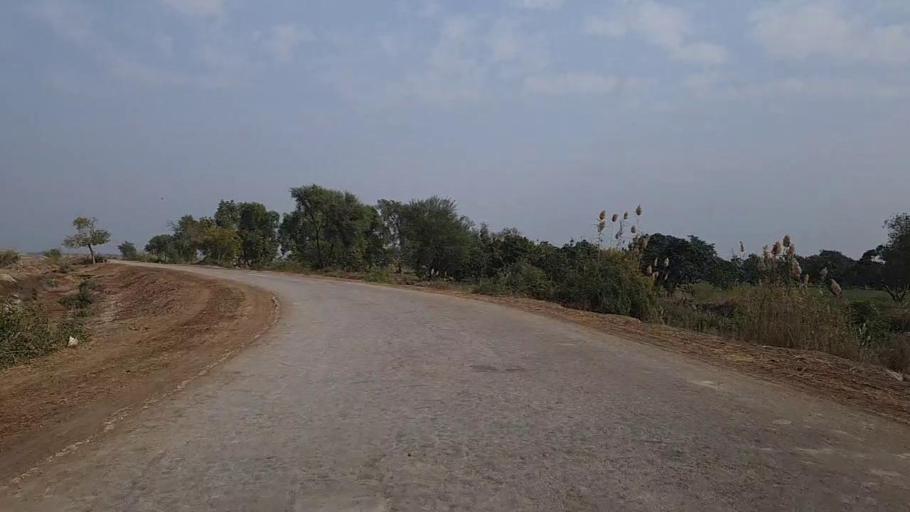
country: PK
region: Sindh
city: Mirwah Gorchani
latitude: 25.3806
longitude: 69.0824
